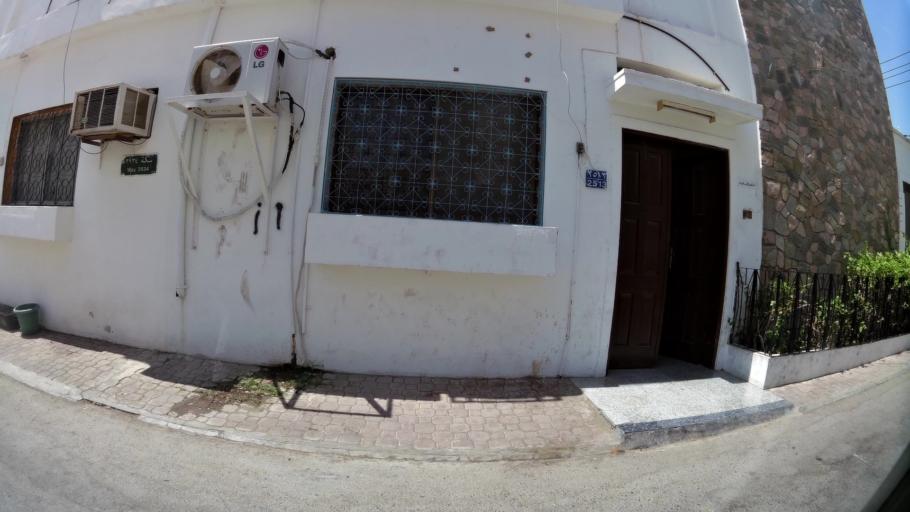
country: OM
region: Muhafazat Masqat
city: Muscat
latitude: 23.6015
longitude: 58.5401
